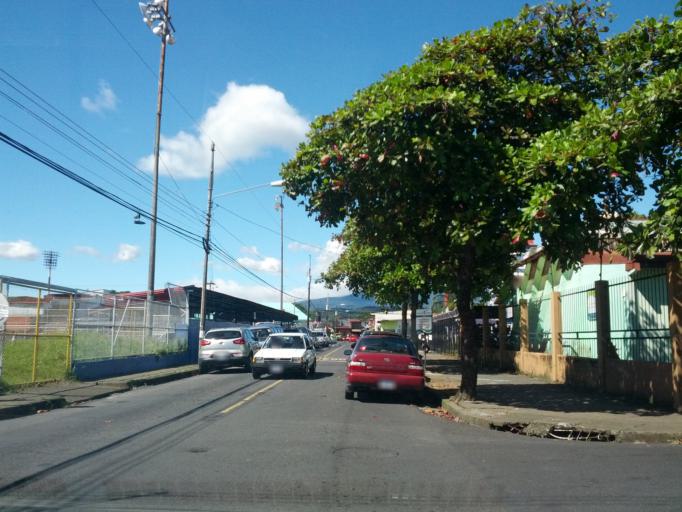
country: CR
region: Alajuela
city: Alajuela
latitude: 10.0197
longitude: -84.2071
